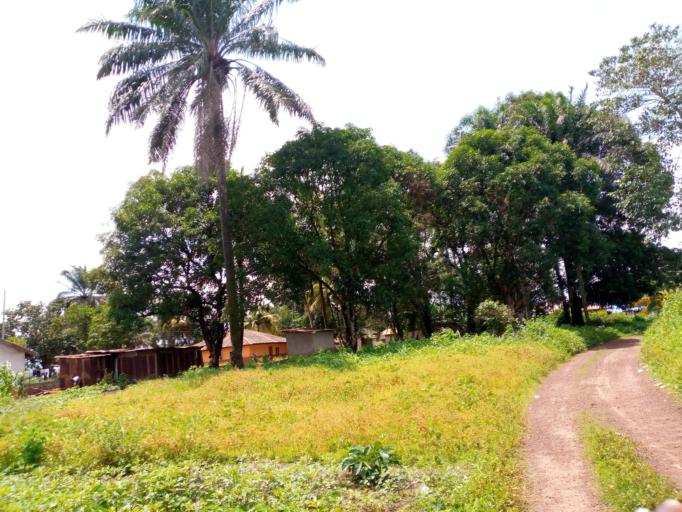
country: SL
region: Northern Province
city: Magburaka
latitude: 8.7253
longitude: -11.9255
